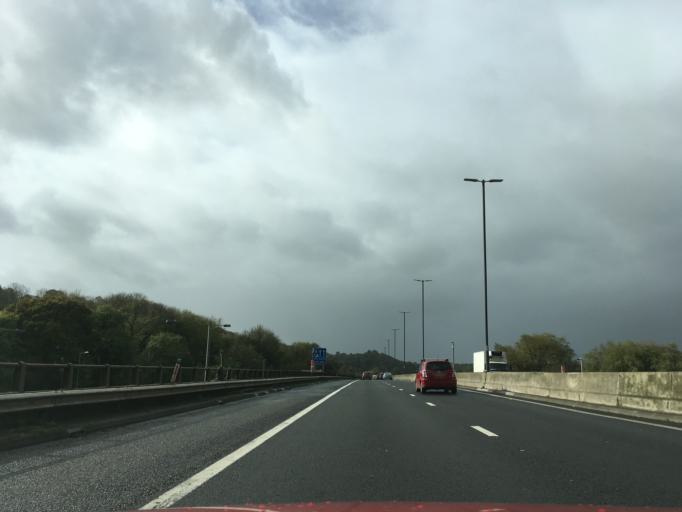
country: GB
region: Wales
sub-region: Newport
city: Newport
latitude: 51.6016
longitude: -3.0036
